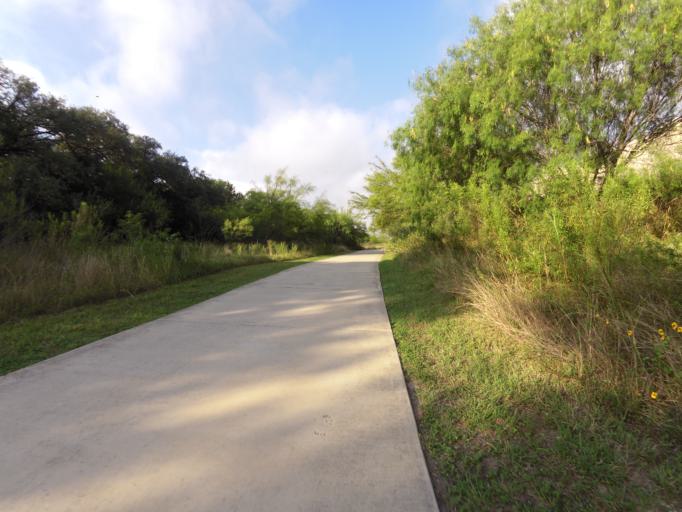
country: US
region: Texas
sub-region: Bexar County
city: Leon Valley
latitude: 29.5148
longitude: -98.6319
